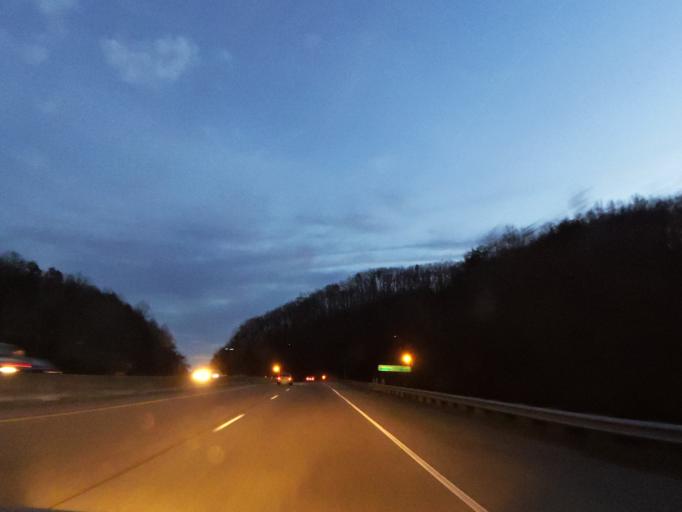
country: US
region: Tennessee
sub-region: Roane County
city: Oliver Springs
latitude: 36.0440
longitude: -84.3381
